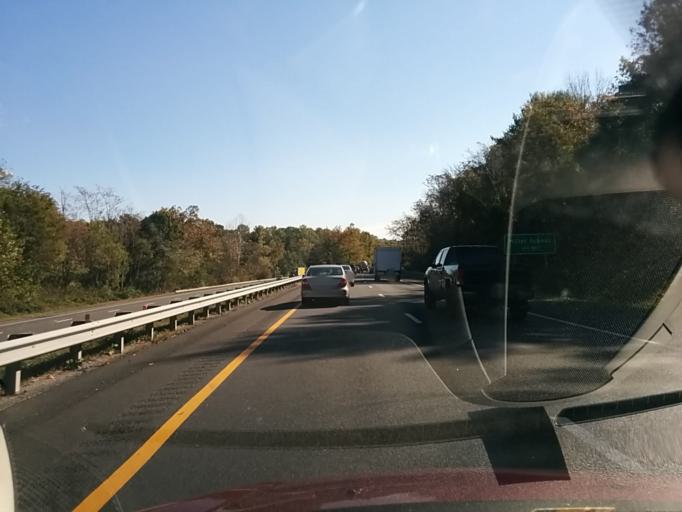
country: US
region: Virginia
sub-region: Albemarle County
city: Crozet
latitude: 38.0468
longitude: -78.7408
